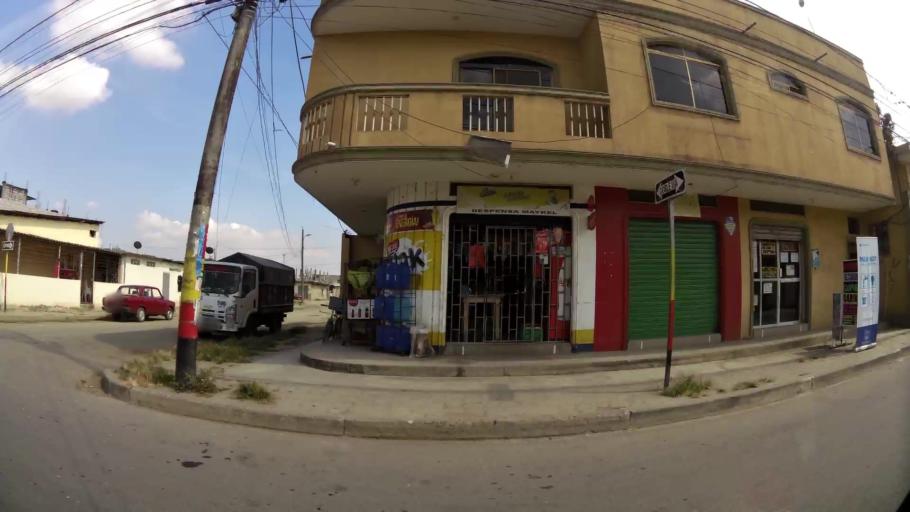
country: EC
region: Guayas
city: Eloy Alfaro
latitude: -2.1723
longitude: -79.8284
